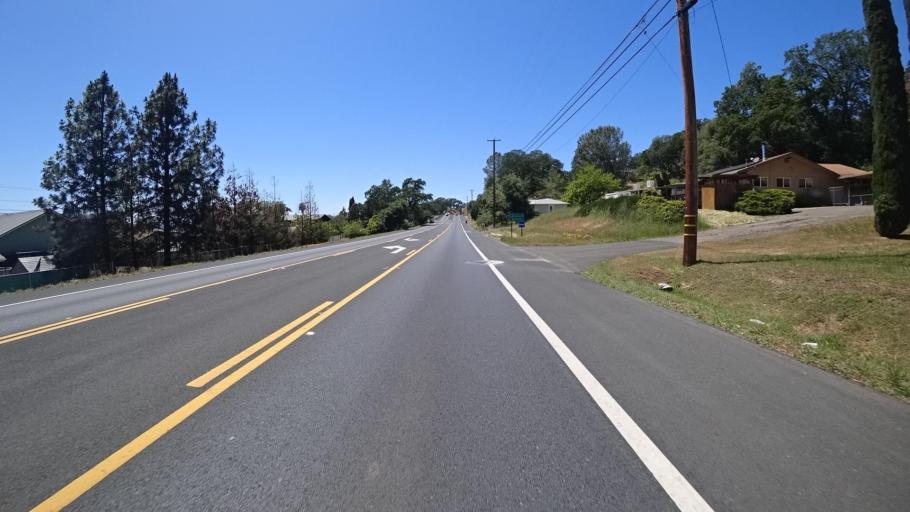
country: US
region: California
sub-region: Lake County
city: Nice
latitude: 39.1229
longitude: -122.8510
